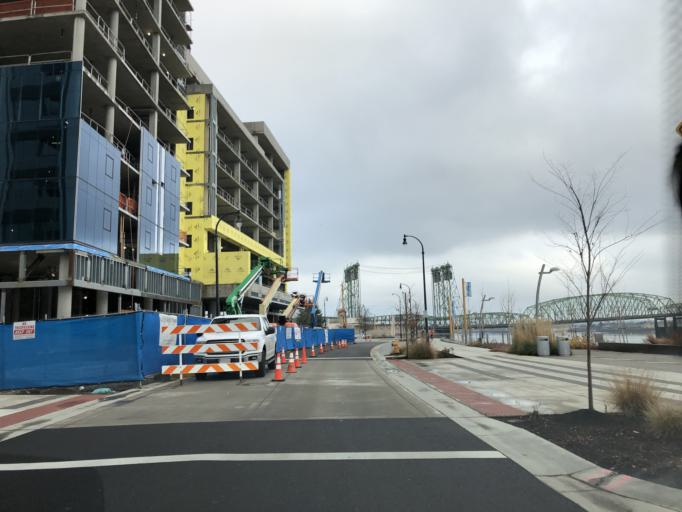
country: US
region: Washington
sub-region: Clark County
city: Vancouver
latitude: 45.6236
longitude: -122.6788
